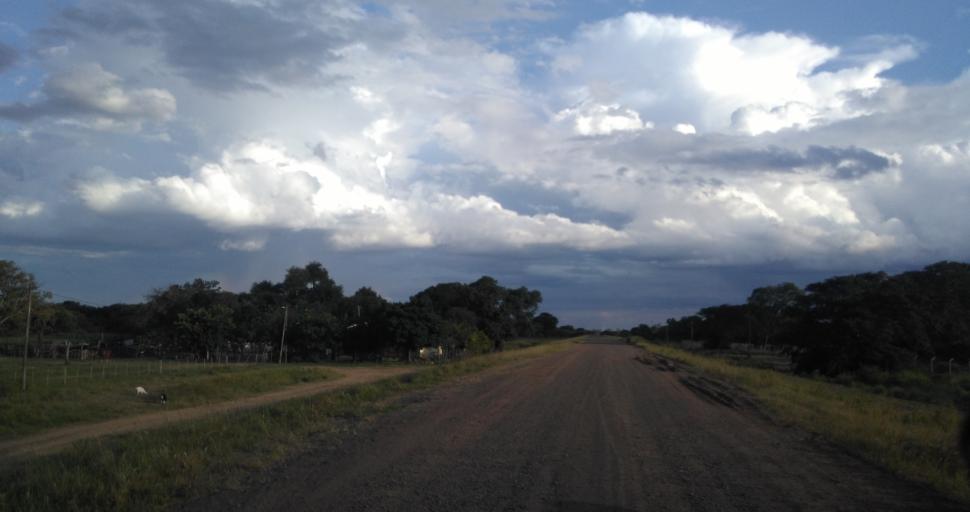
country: AR
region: Chaco
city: Resistencia
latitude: -27.4129
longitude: -58.9432
